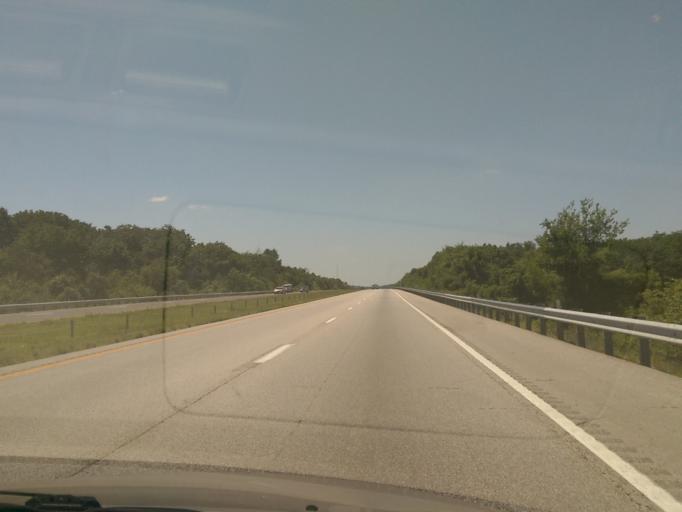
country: US
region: Missouri
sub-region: Cooper County
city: Boonville
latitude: 38.9336
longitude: -92.9634
